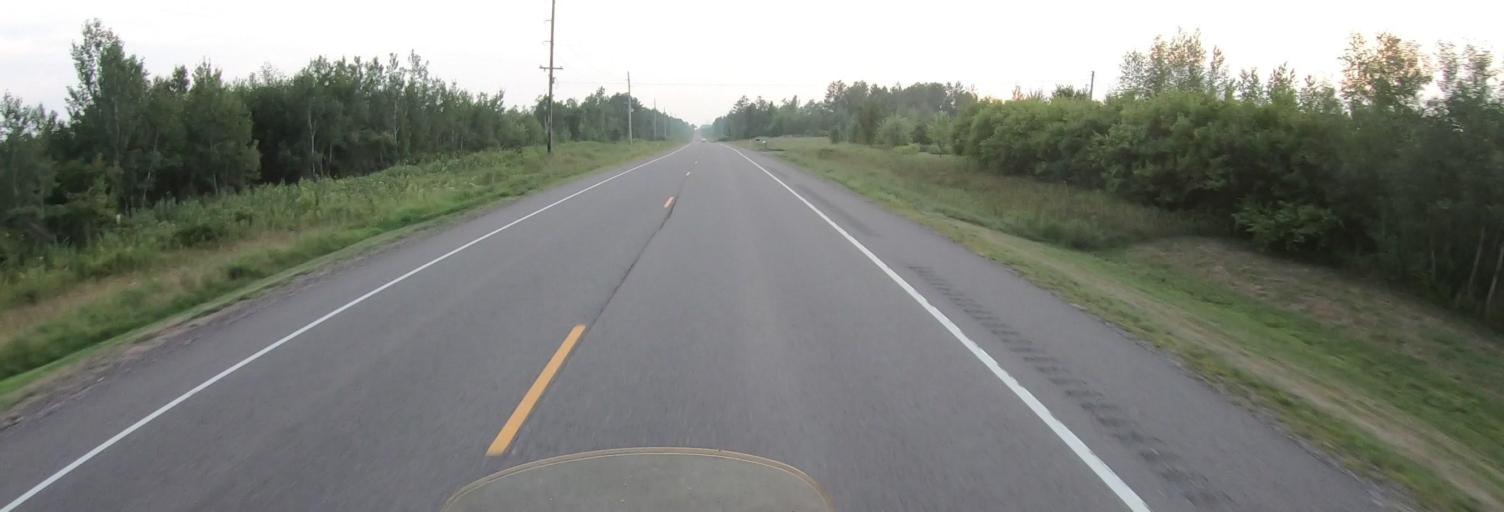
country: US
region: Wisconsin
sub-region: Burnett County
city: Grantsburg
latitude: 45.7738
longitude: -92.7949
